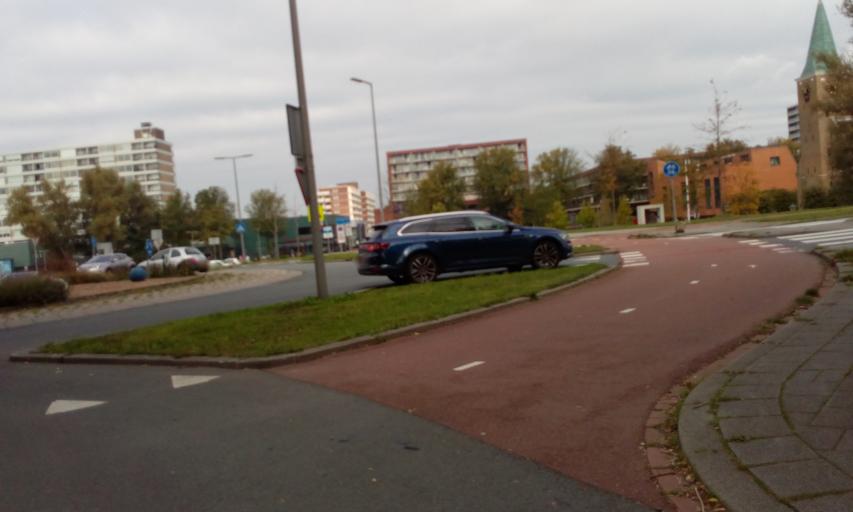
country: NL
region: South Holland
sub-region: Gemeente Spijkenisse
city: Spijkenisse
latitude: 51.8637
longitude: 4.3583
